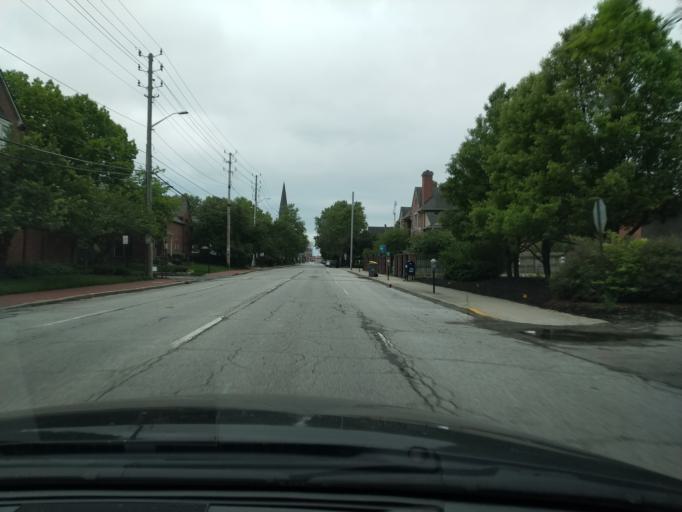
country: US
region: Indiana
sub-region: Marion County
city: Indianapolis
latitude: 39.7733
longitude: -86.1488
